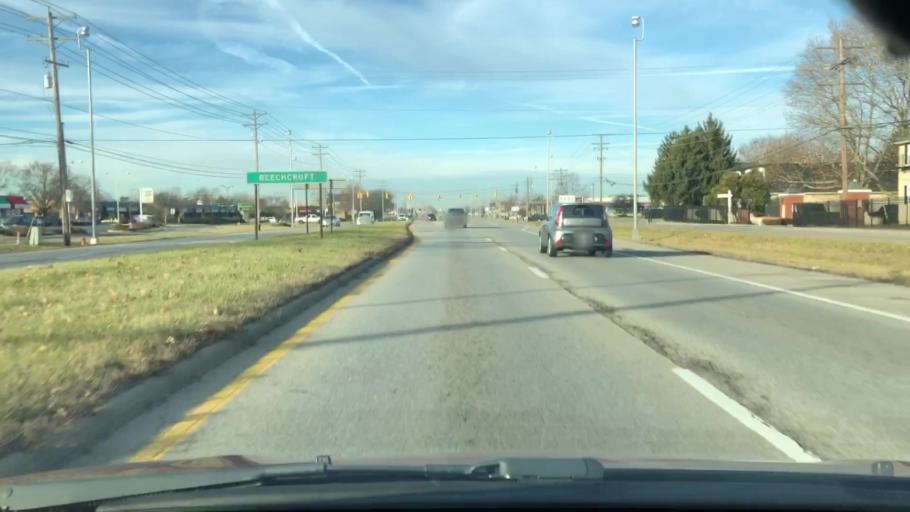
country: US
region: Ohio
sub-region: Franklin County
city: Minerva Park
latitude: 40.0869
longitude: -82.9626
